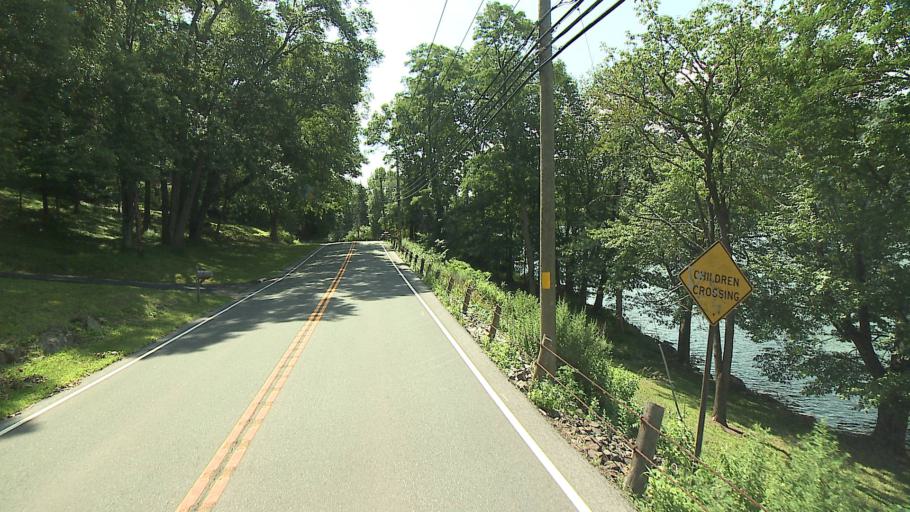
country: US
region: Connecticut
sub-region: Fairfield County
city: Sherman
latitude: 41.5192
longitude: -73.4779
